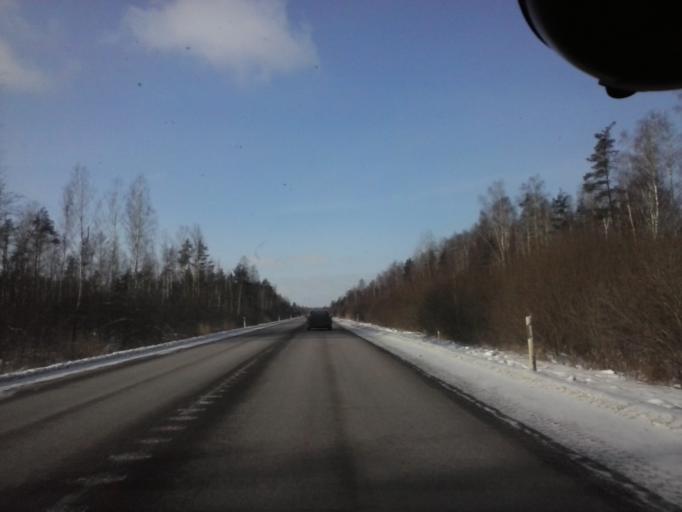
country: EE
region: Tartu
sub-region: Noo vald
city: Noo
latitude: 58.3455
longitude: 26.4800
